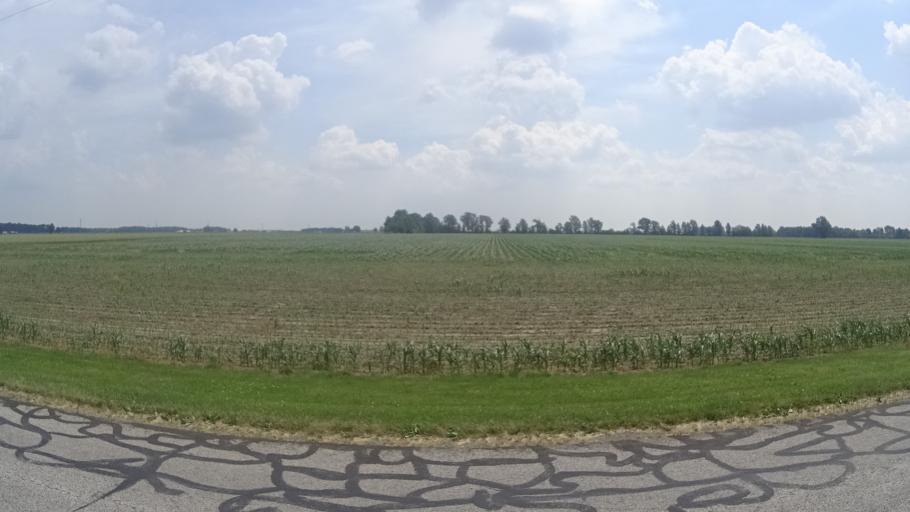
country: US
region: Ohio
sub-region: Huron County
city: Monroeville
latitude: 41.3285
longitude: -82.6934
